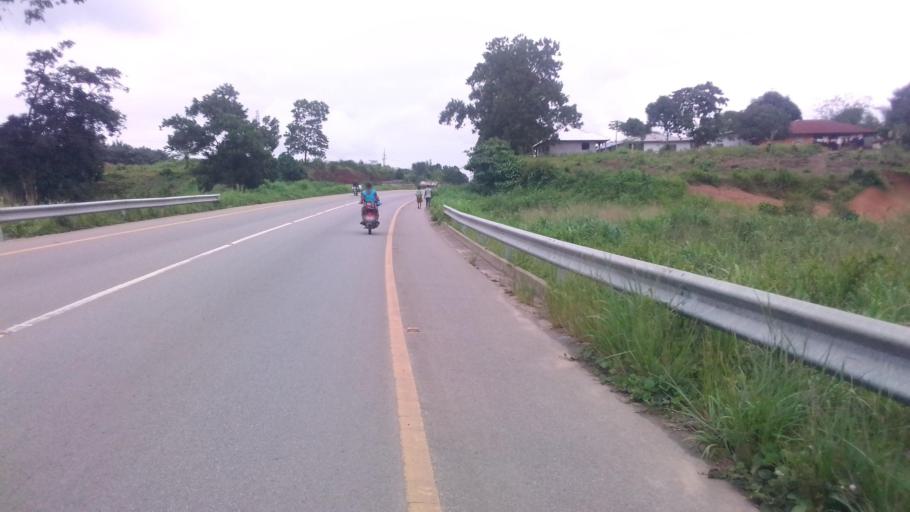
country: SL
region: Eastern Province
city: Hangha
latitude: 7.9196
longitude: -11.1597
